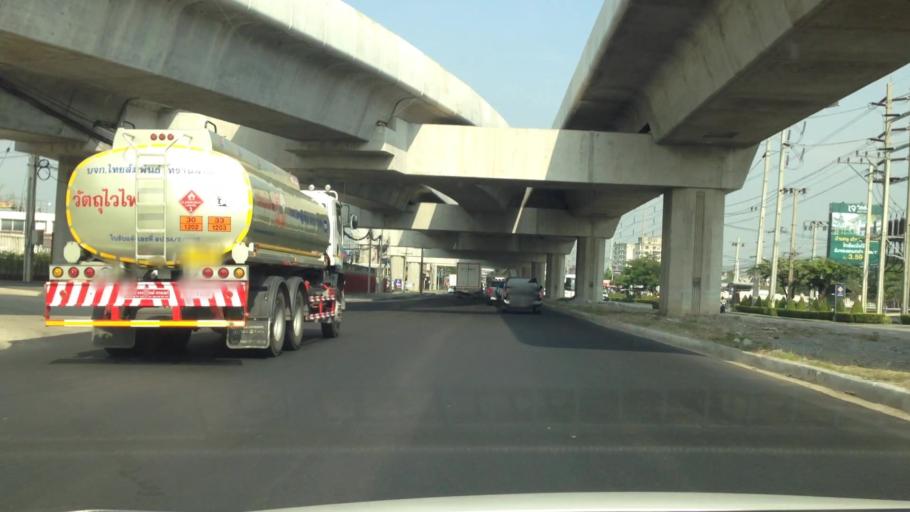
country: TH
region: Samut Prakan
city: Samut Prakan
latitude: 13.5578
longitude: 100.6124
